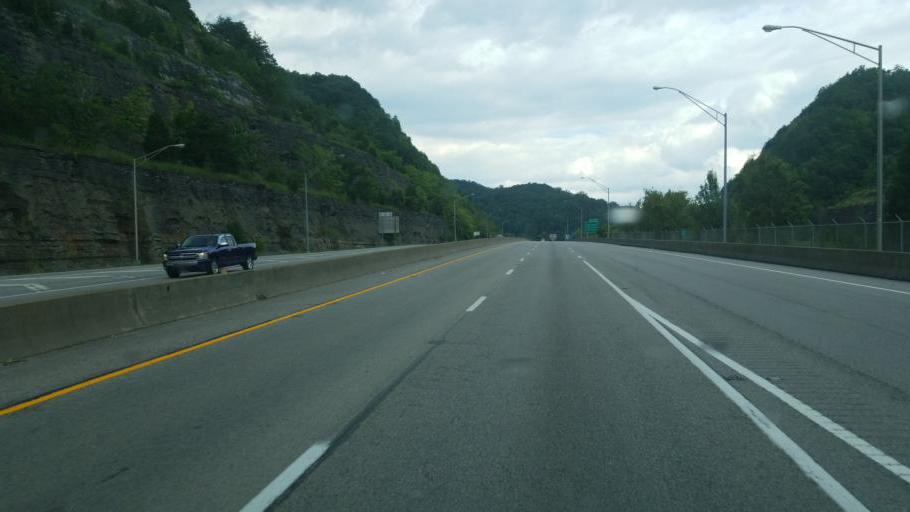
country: US
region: Kentucky
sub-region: Pike County
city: Pikeville
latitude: 37.4781
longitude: -82.5416
